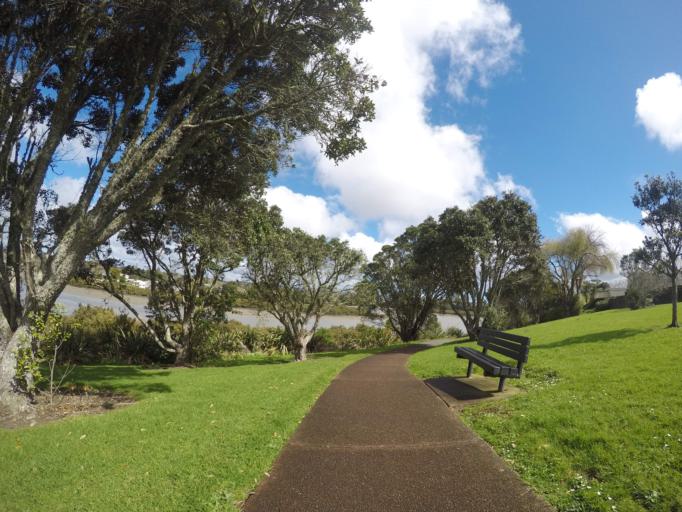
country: NZ
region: Auckland
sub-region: Auckland
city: Rosebank
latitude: -36.8978
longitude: 174.6792
